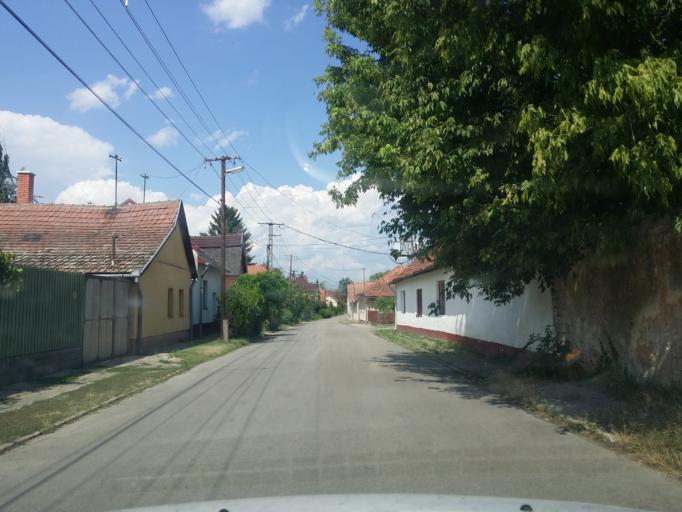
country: HU
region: Bacs-Kiskun
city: Jaszszentlaszlo
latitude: 46.5689
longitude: 19.7606
